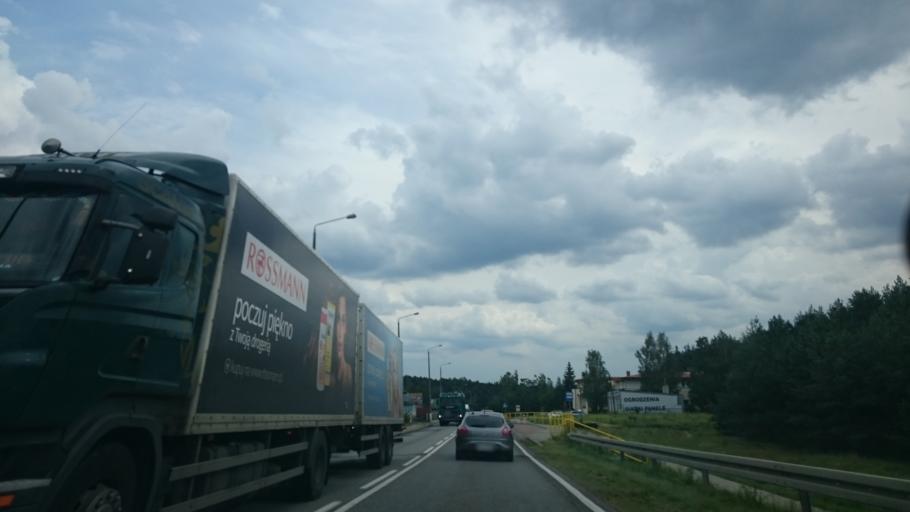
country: PL
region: Kujawsko-Pomorskie
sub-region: Powiat tucholski
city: Tuchola
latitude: 53.5663
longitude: 17.8953
